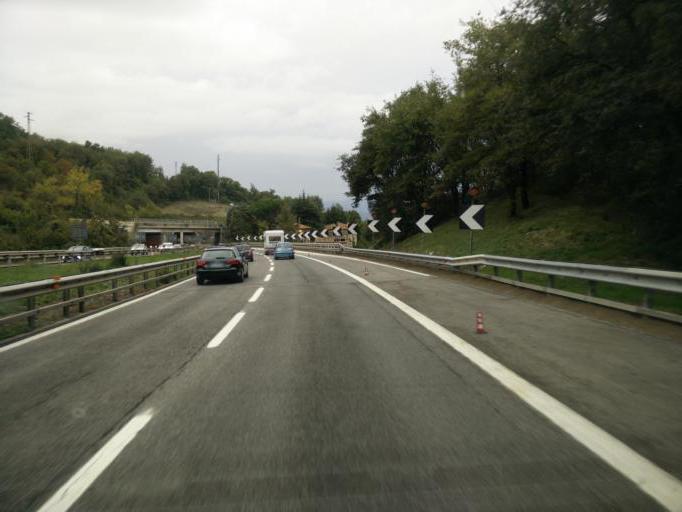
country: IT
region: Tuscany
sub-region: Province of Florence
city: Cavallina
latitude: 43.9507
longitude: 11.2137
